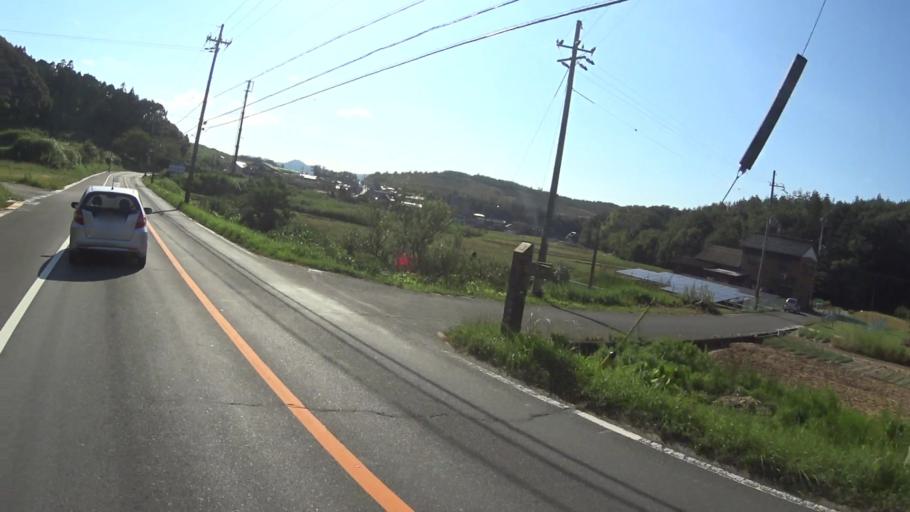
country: JP
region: Kyoto
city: Miyazu
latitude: 35.6992
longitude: 135.0602
